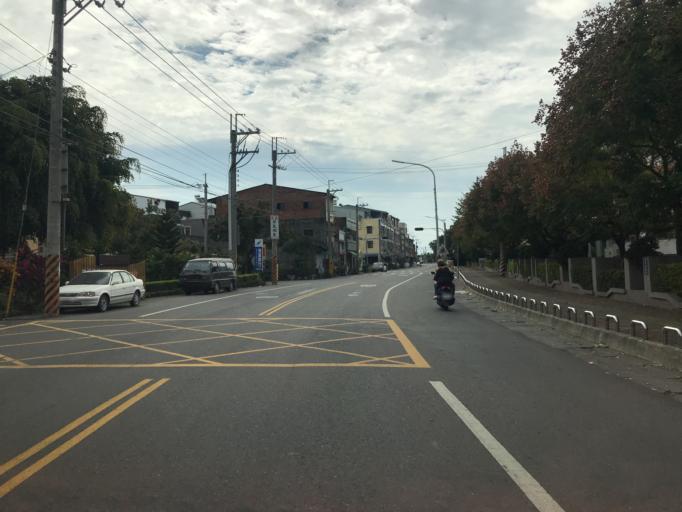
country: TW
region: Taiwan
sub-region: Nantou
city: Nantou
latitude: 23.8897
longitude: 120.5874
